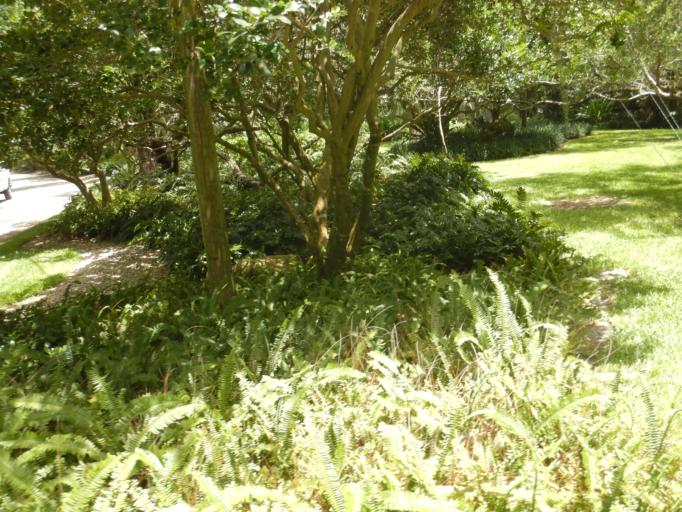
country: US
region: Florida
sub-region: Sarasota County
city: Gulf Gate Estates
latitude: 27.2364
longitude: -82.5255
